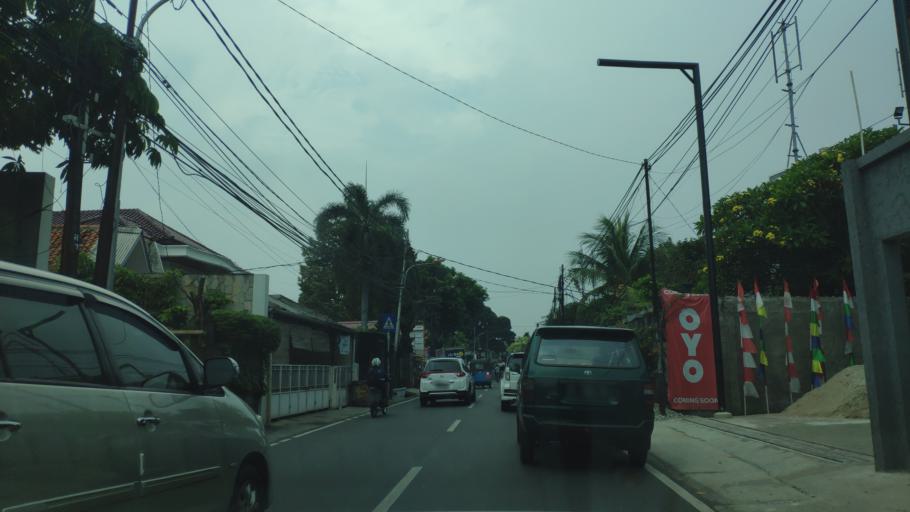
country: ID
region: Jakarta Raya
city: Jakarta
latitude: -6.1912
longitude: 106.7856
